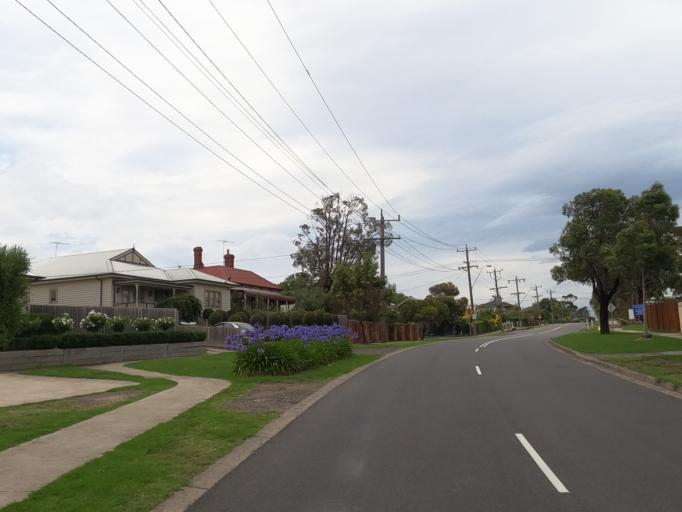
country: AU
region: Victoria
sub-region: Hume
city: Westmeadows
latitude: -37.6768
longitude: 144.8916
